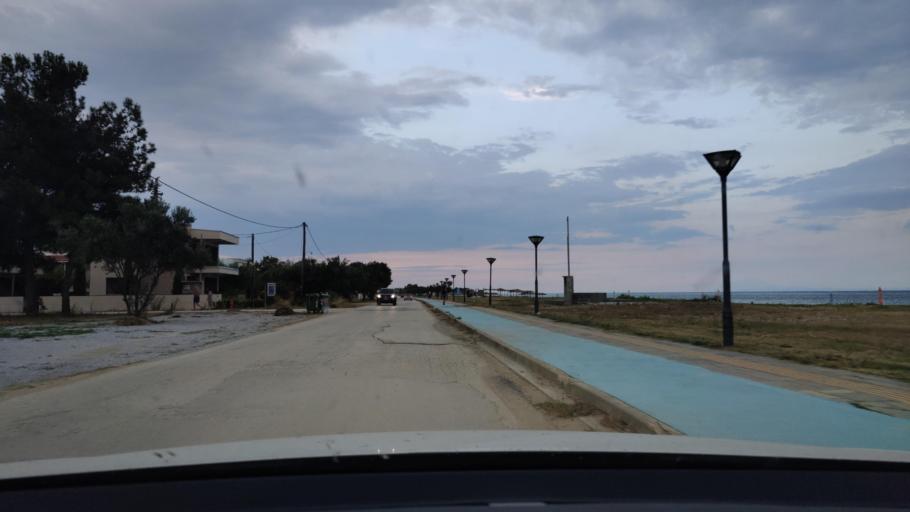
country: GR
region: East Macedonia and Thrace
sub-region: Nomos Kavalas
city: Paralia Ofryniou
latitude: 40.7703
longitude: 23.8893
